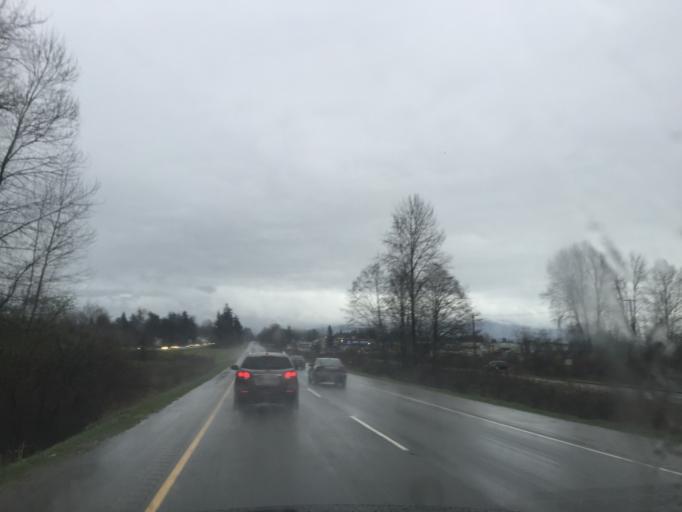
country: CA
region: British Columbia
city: Aldergrove
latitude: 49.0515
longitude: -122.3670
